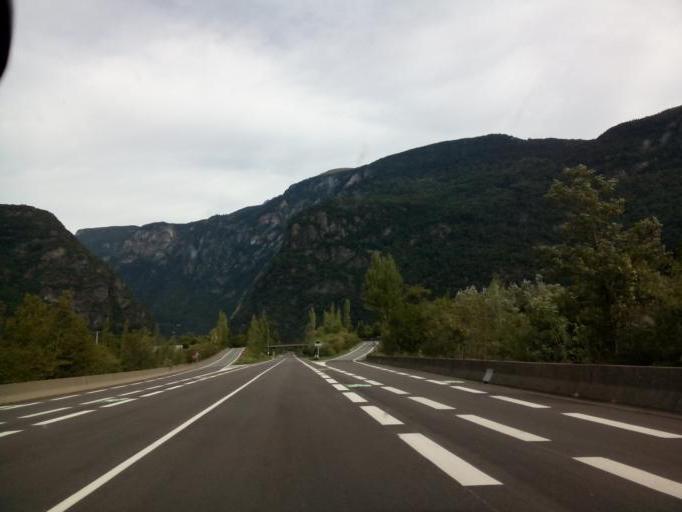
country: FR
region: Rhone-Alpes
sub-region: Departement de l'Isere
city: Vaulnaveys-le-Bas
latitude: 45.0539
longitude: 5.8188
